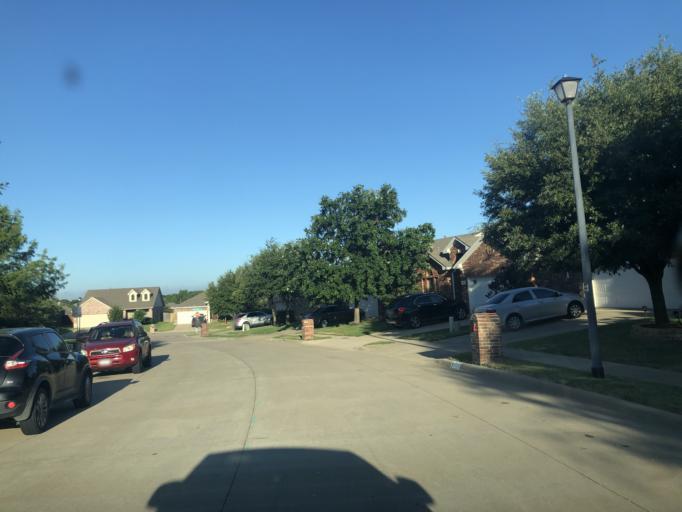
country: US
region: Texas
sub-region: Dallas County
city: Duncanville
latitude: 32.6512
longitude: -96.9484
